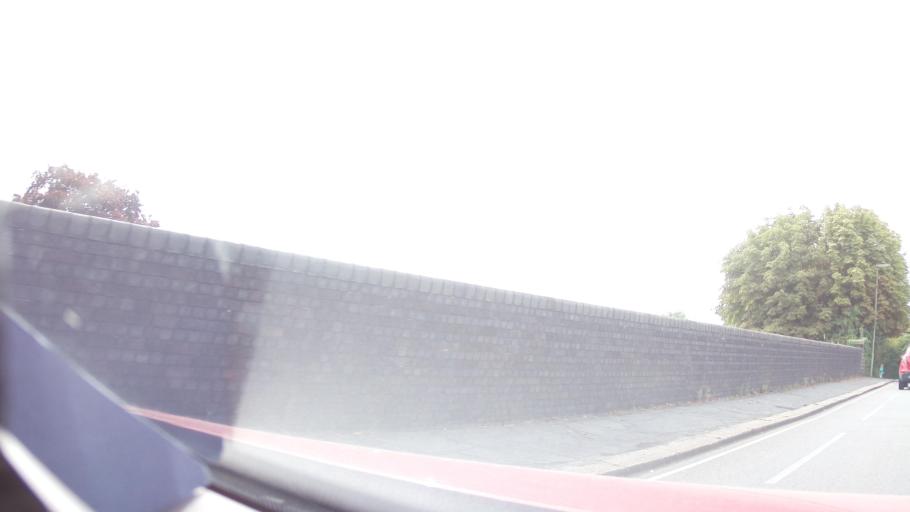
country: GB
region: England
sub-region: Surrey
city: Horley
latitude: 51.1696
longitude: -0.1605
